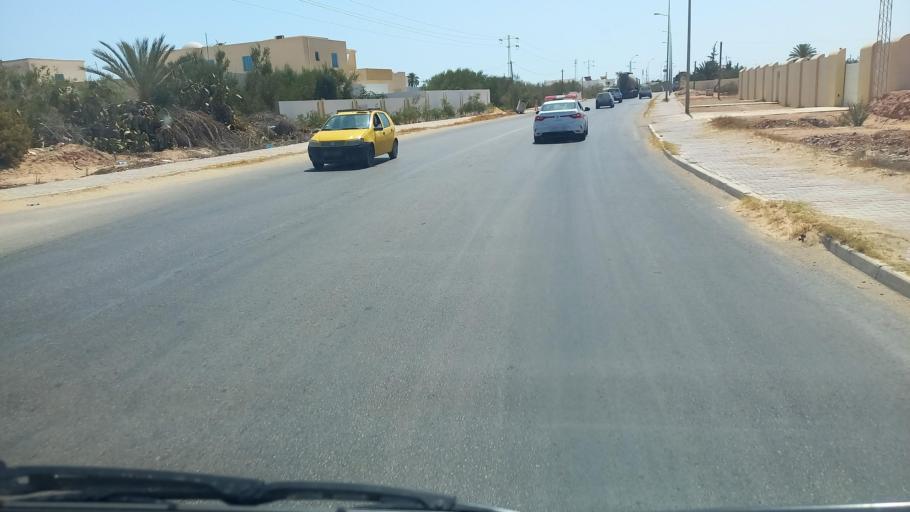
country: TN
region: Madanin
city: Houmt Souk
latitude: 33.7803
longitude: 10.8907
